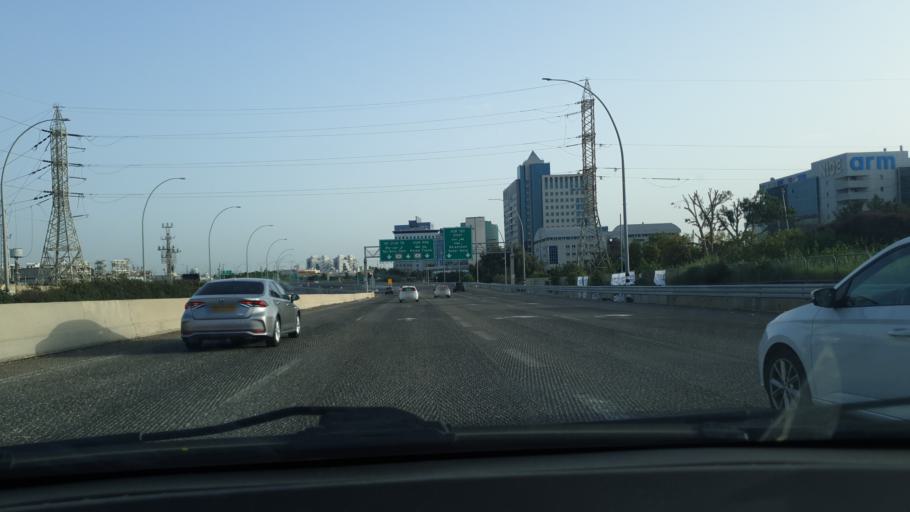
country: IL
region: Central District
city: Ra'anana
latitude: 32.2002
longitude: 34.8846
